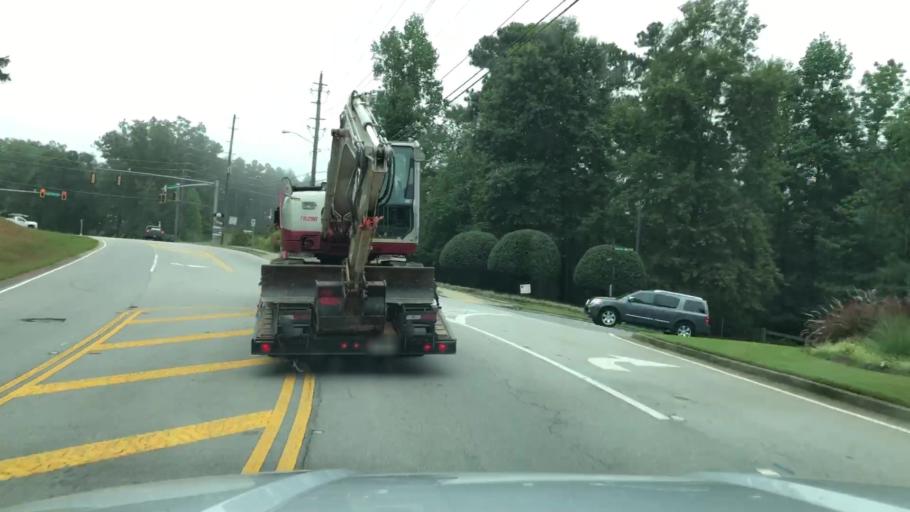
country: US
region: Georgia
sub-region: Bartow County
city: Emerson
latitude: 34.0394
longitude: -84.7737
